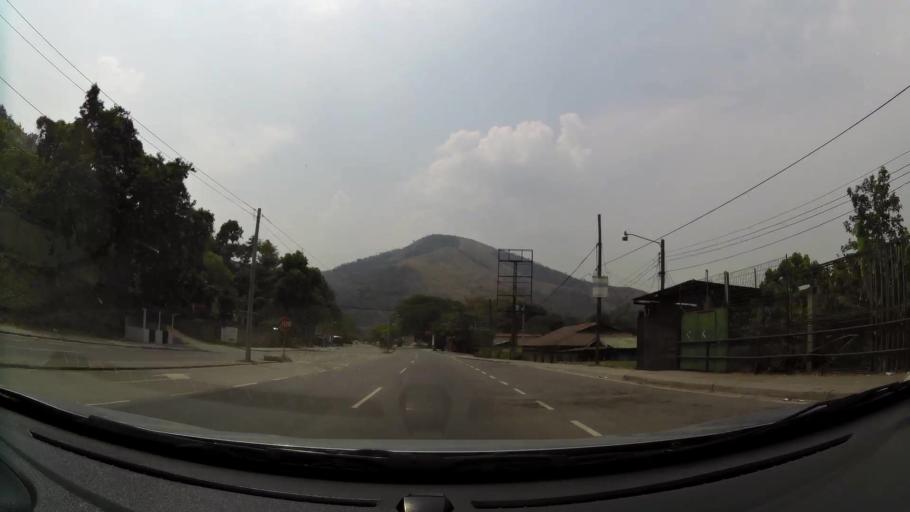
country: HN
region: Cortes
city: El Maranon
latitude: 15.4241
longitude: -88.0207
